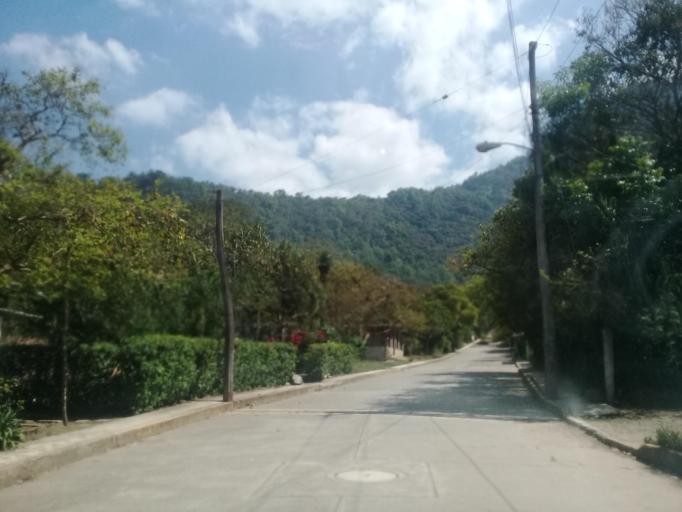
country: MX
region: Veracruz
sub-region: Tlilapan
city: Tonalixco
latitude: 18.8029
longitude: -97.0709
